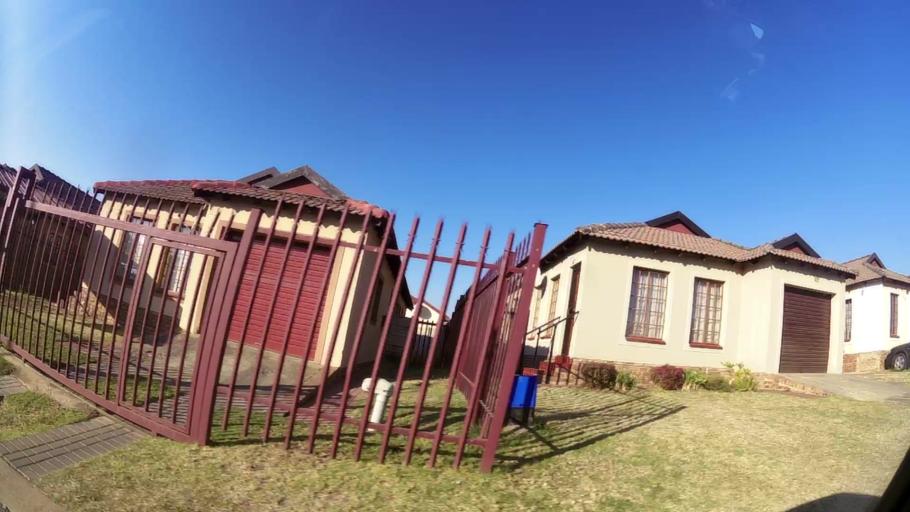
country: ZA
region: Gauteng
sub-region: City of Johannesburg Metropolitan Municipality
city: Midrand
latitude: -25.9103
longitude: 28.1023
